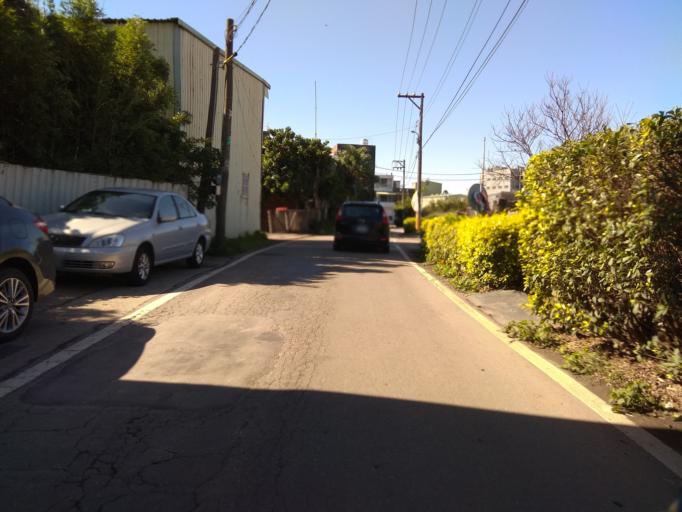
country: TW
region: Taiwan
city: Taoyuan City
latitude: 24.9664
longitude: 121.1505
